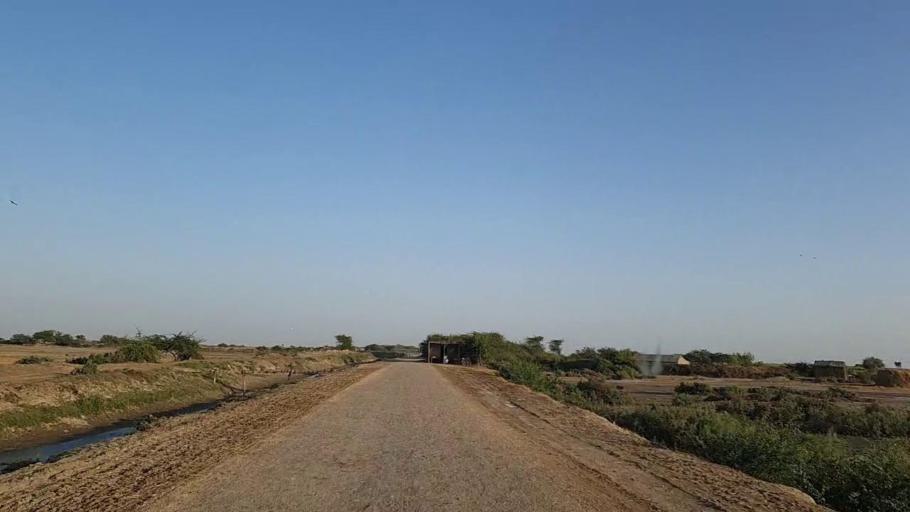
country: PK
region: Sindh
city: Jati
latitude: 24.4057
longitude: 68.3544
